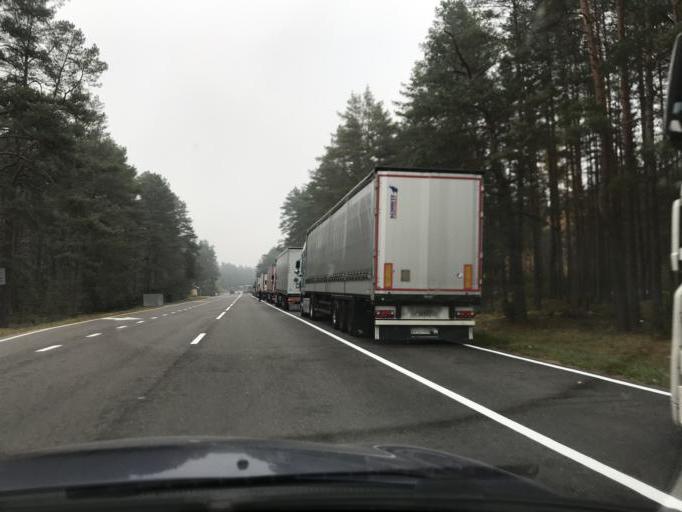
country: LT
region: Alytaus apskritis
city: Druskininkai
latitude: 53.9272
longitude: 23.9351
